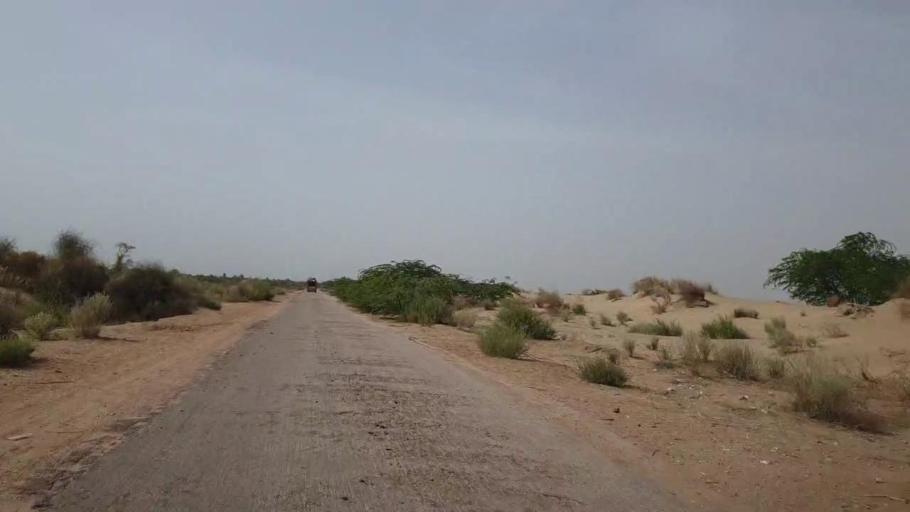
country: PK
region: Sindh
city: Bandhi
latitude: 26.5620
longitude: 68.3816
